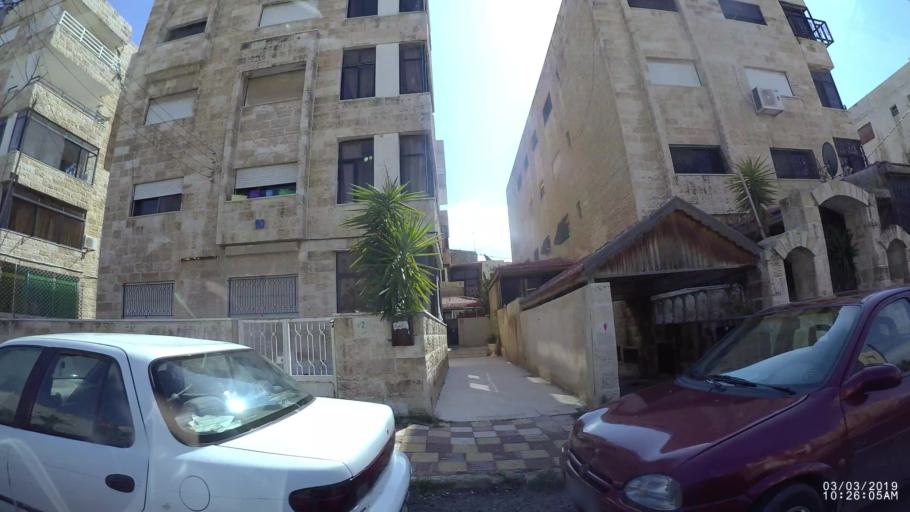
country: JO
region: Amman
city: Al Jubayhah
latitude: 31.9890
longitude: 35.9003
